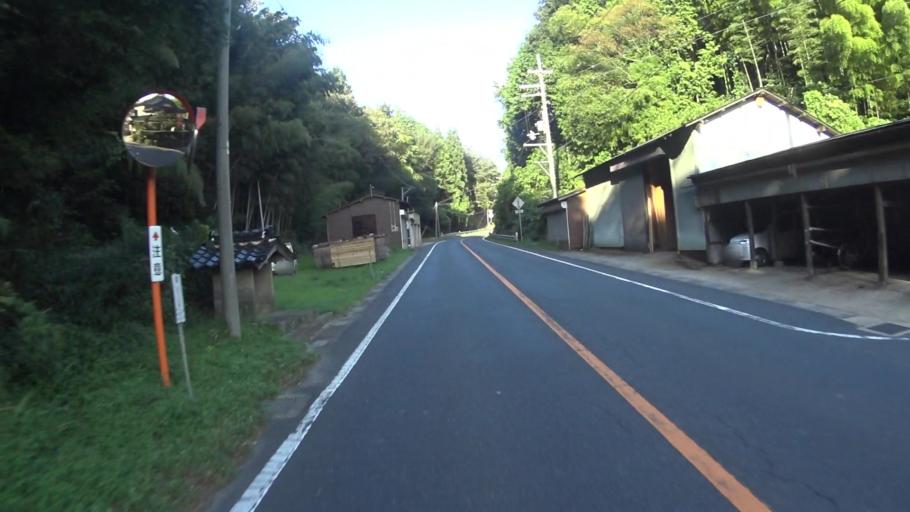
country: JP
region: Hyogo
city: Toyooka
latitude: 35.5938
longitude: 134.9070
